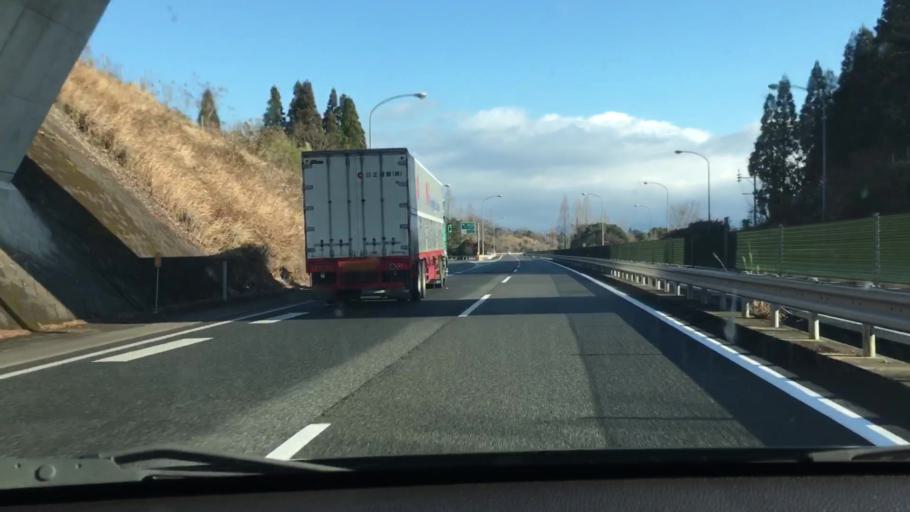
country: JP
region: Kumamoto
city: Hitoyoshi
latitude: 32.2336
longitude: 130.7675
